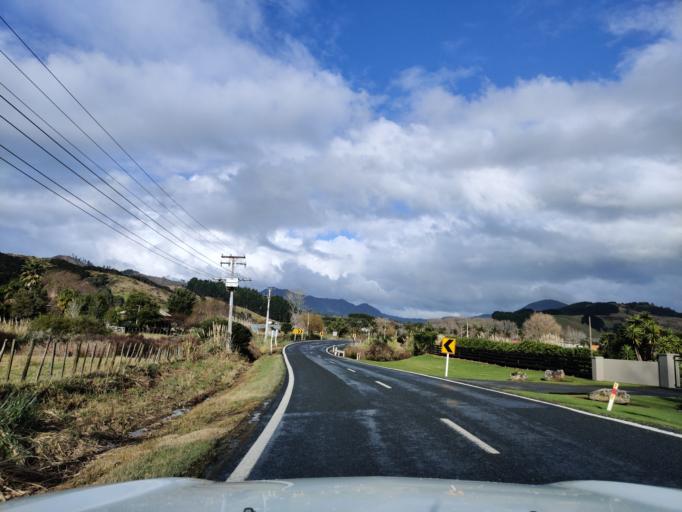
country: NZ
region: Waikato
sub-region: Thames-Coromandel District
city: Coromandel
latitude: -36.7804
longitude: 175.5104
